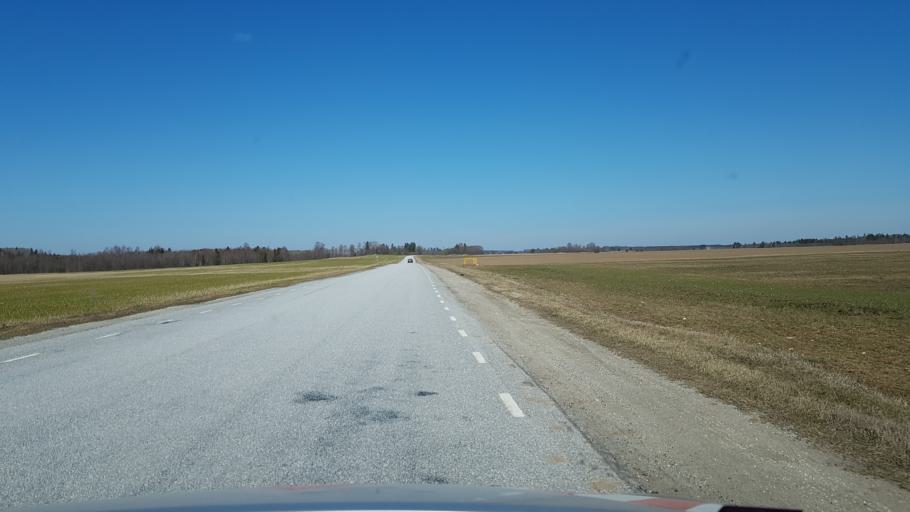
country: EE
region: Jaervamaa
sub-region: Koeru vald
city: Koeru
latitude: 59.0064
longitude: 26.0901
